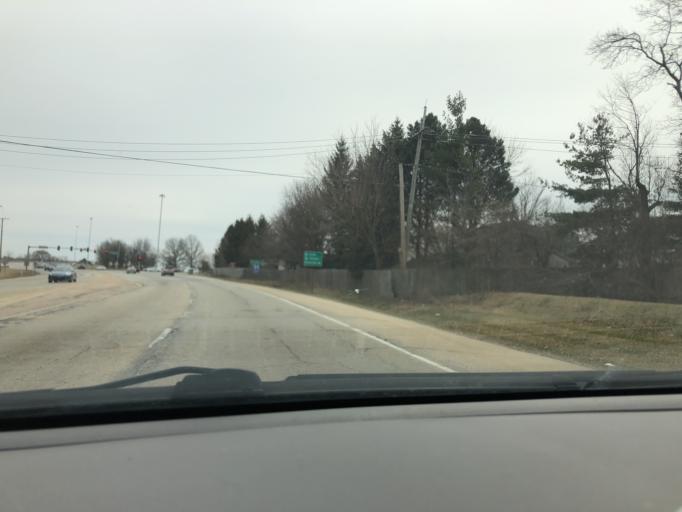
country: US
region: Illinois
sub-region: Kane County
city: Elgin
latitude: 42.0364
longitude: -88.3410
